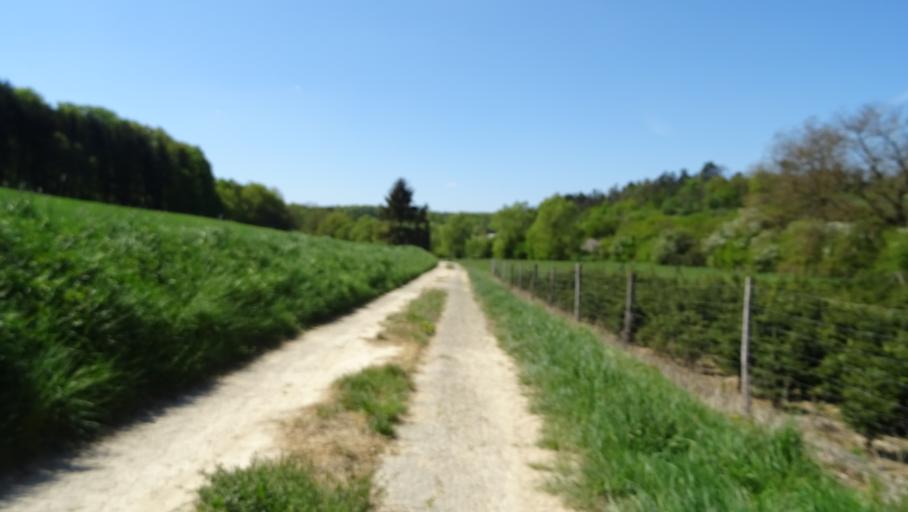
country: DE
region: Baden-Wuerttemberg
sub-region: Karlsruhe Region
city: Limbach
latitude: 49.4142
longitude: 9.2477
